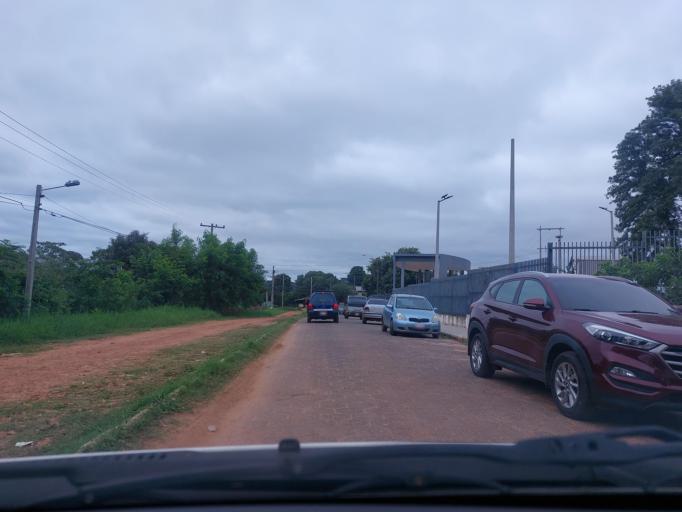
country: PY
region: San Pedro
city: Guayaybi
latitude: -24.6649
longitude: -56.4311
